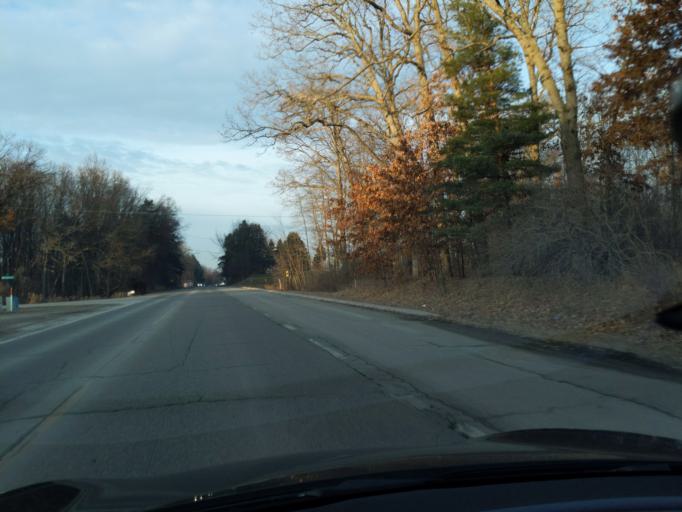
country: US
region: Michigan
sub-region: Livingston County
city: Brighton
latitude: 42.5886
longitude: -83.7538
